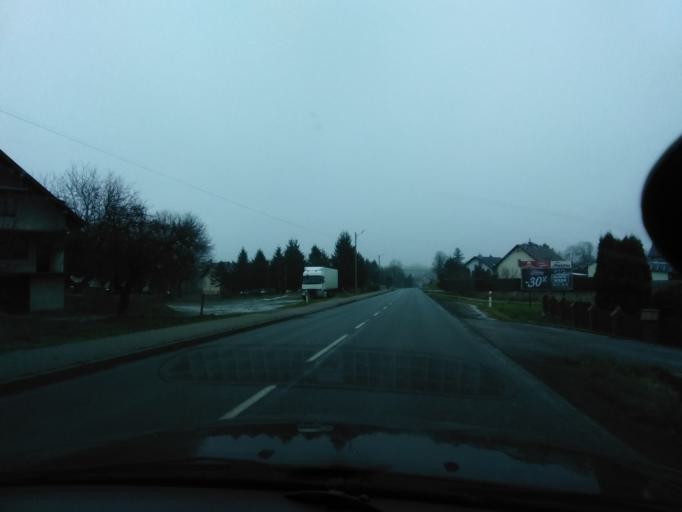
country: PL
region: Subcarpathian Voivodeship
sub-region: Powiat lancucki
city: Sonina
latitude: 50.0577
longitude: 22.2645
